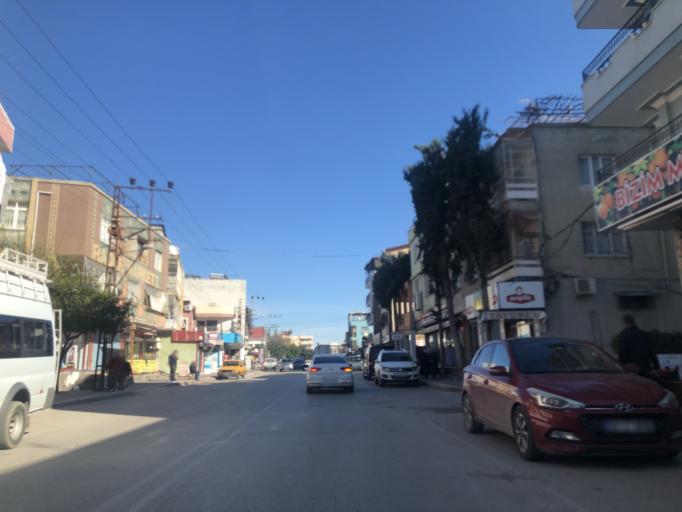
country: TR
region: Adana
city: Yuregir
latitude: 37.0089
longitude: 35.3653
